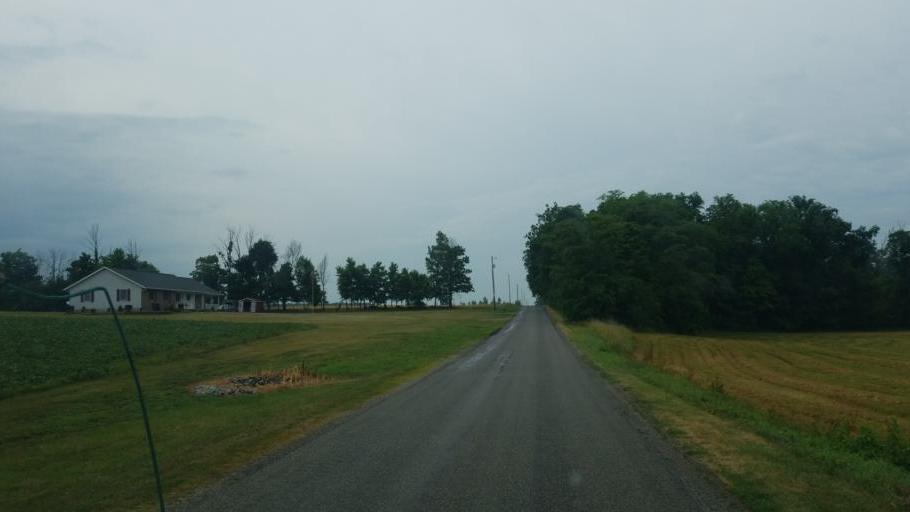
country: US
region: Ohio
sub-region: Williams County
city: Edgerton
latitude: 41.4026
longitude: -84.6701
